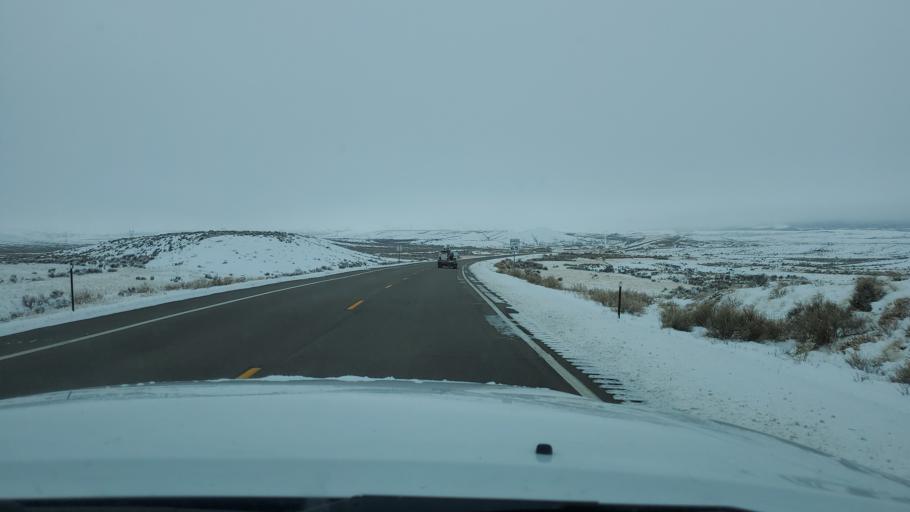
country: US
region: Colorado
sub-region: Rio Blanco County
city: Rangely
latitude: 40.3030
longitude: -108.5255
